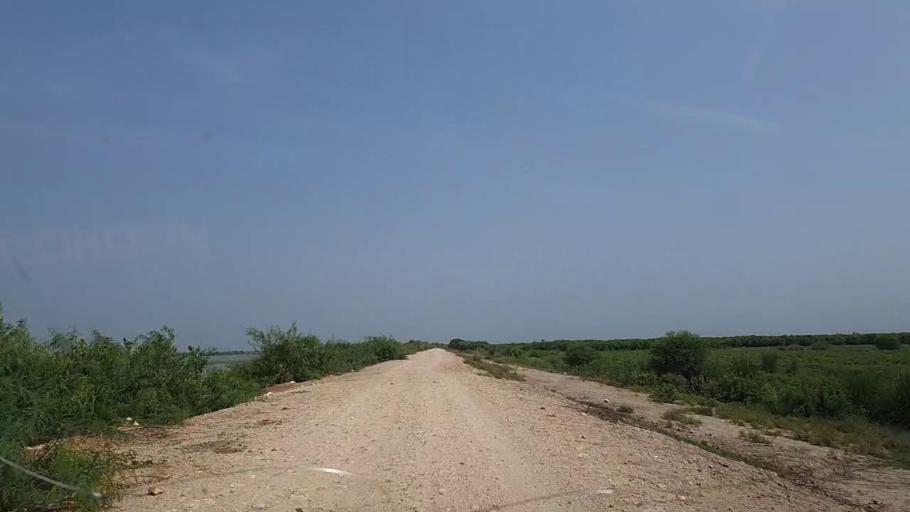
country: PK
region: Sindh
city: Ghotki
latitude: 28.1028
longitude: 69.3992
